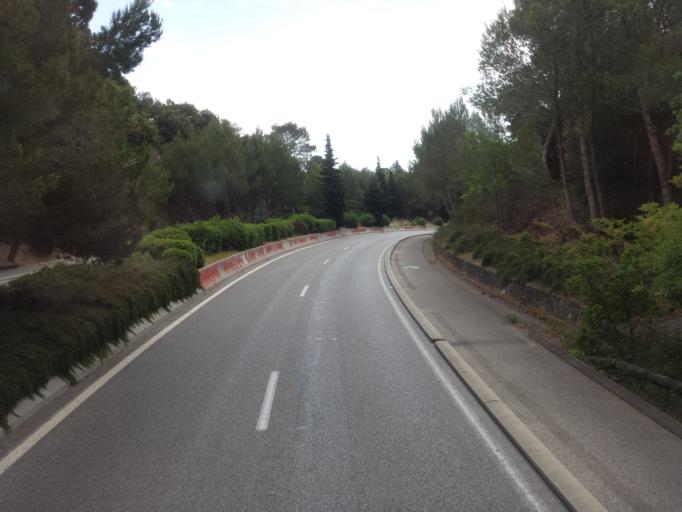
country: FR
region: Provence-Alpes-Cote d'Azur
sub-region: Departement des Alpes-Maritimes
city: Biot
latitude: 43.6114
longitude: 7.0798
